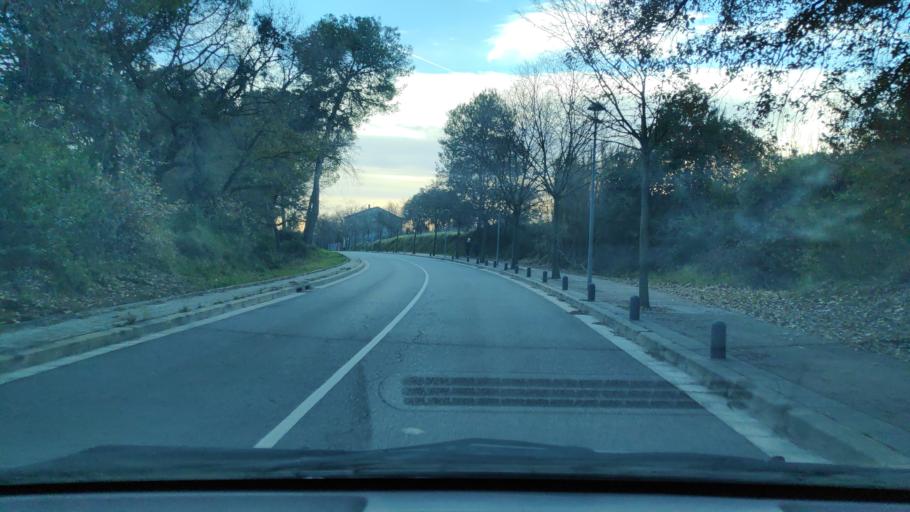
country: ES
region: Catalonia
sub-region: Provincia de Barcelona
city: Montmelo
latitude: 41.5645
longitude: 2.2591
